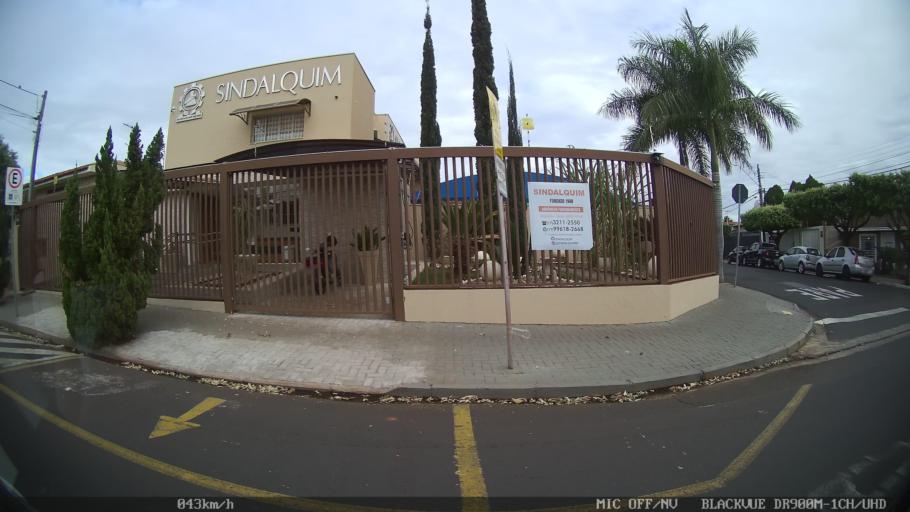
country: BR
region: Sao Paulo
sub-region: Sao Jose Do Rio Preto
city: Sao Jose do Rio Preto
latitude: -20.8201
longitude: -49.3714
